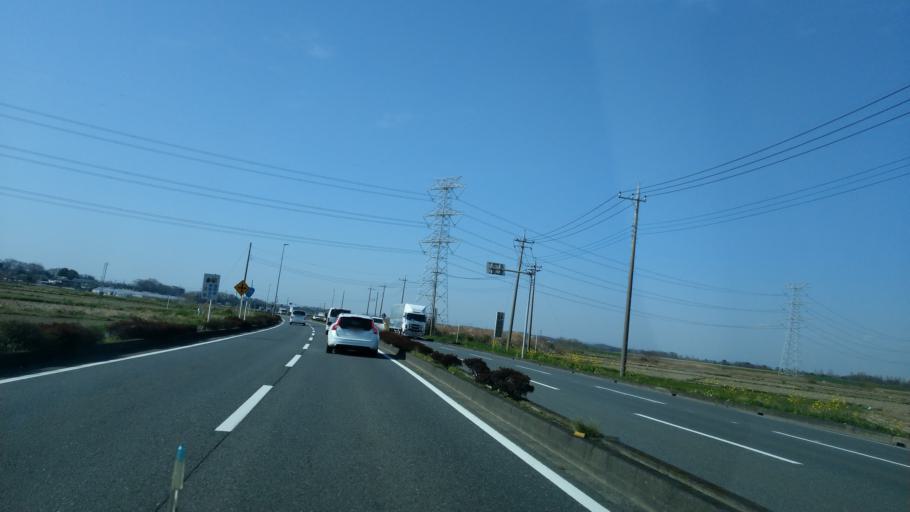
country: JP
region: Saitama
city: Sakado
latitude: 36.0020
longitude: 139.4496
